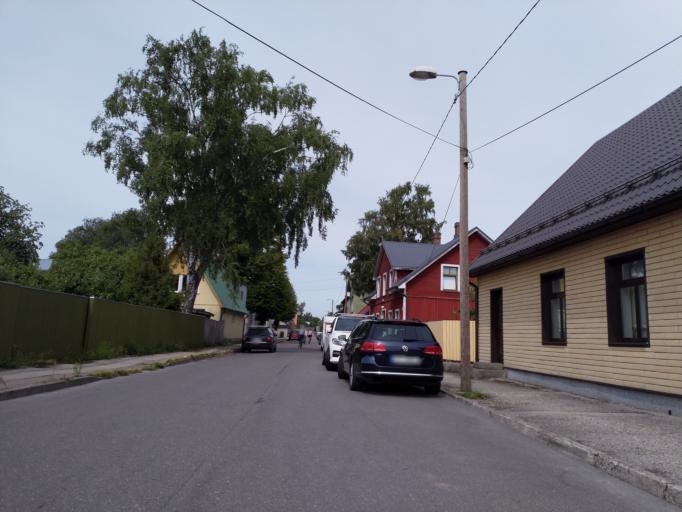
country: EE
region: Paernumaa
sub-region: Paernu linn
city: Parnu
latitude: 58.3787
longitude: 24.5203
